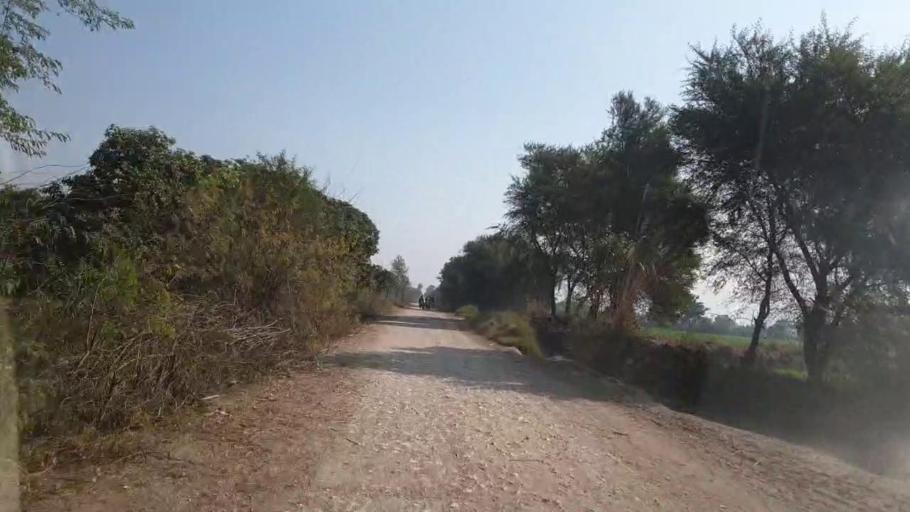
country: PK
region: Sindh
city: Matiari
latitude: 25.5444
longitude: 68.4934
